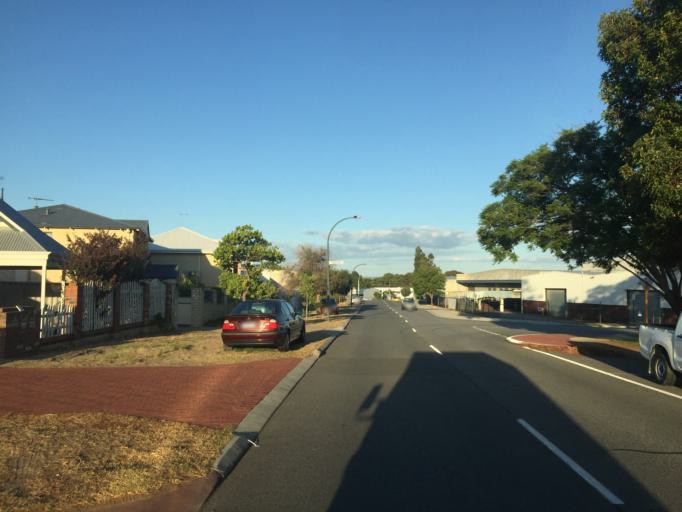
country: AU
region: Western Australia
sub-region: Belmont
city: Rivervale
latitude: -31.9547
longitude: 115.9166
